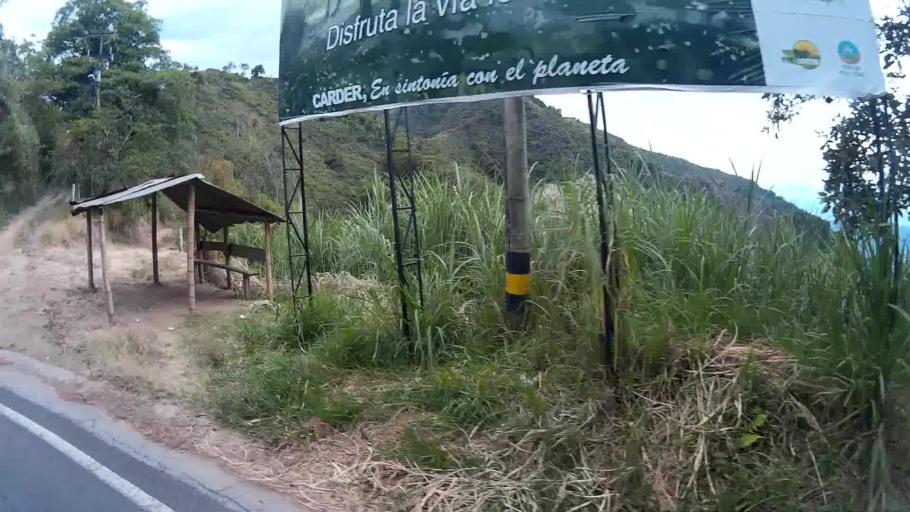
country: CO
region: Risaralda
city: Marsella
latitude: 4.8722
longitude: -75.7652
